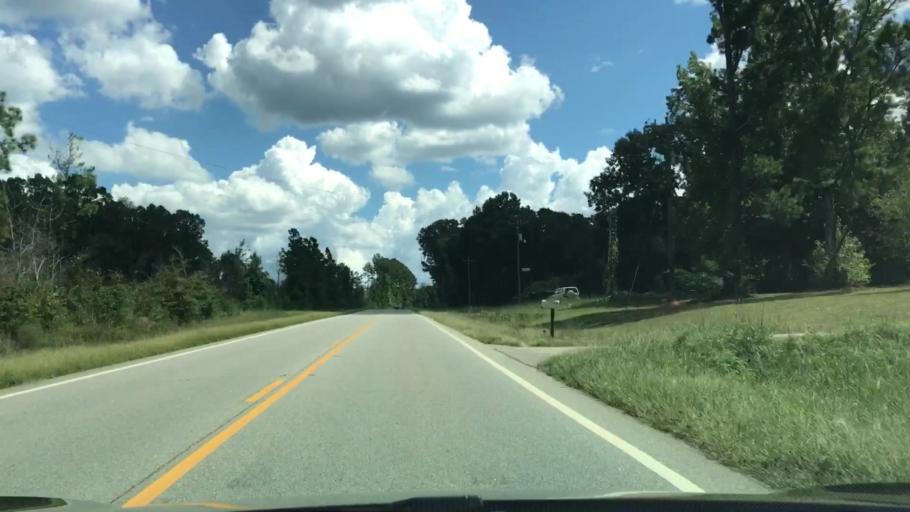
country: US
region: Georgia
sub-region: Greene County
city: Greensboro
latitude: 33.6085
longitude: -83.2028
